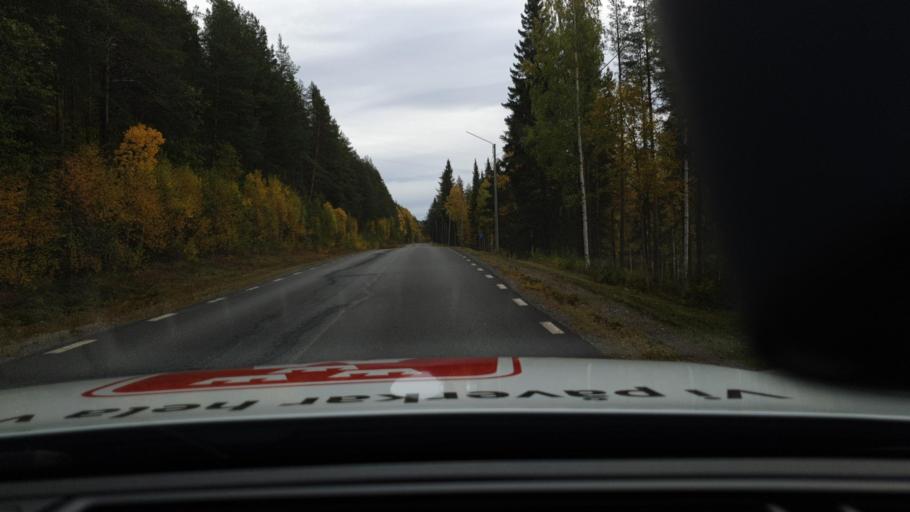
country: SE
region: Vaesterbotten
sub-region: Skelleftea Kommun
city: Langsele
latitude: 64.9458
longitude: 20.0270
